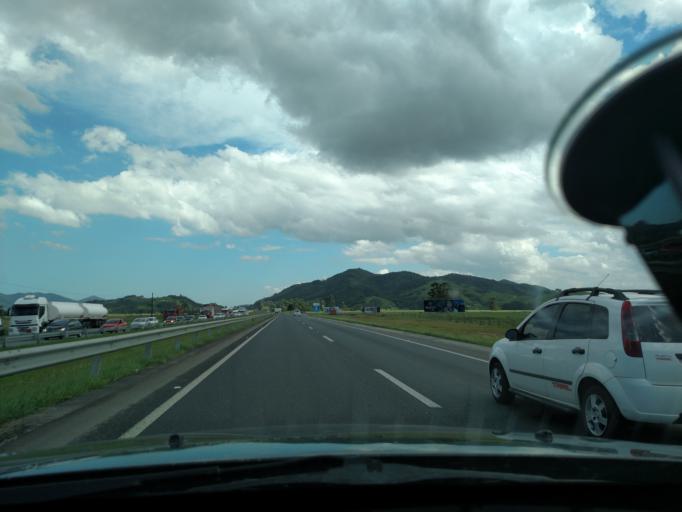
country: BR
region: Santa Catarina
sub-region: Tijucas
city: Tijucas
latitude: -27.2624
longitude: -48.6318
